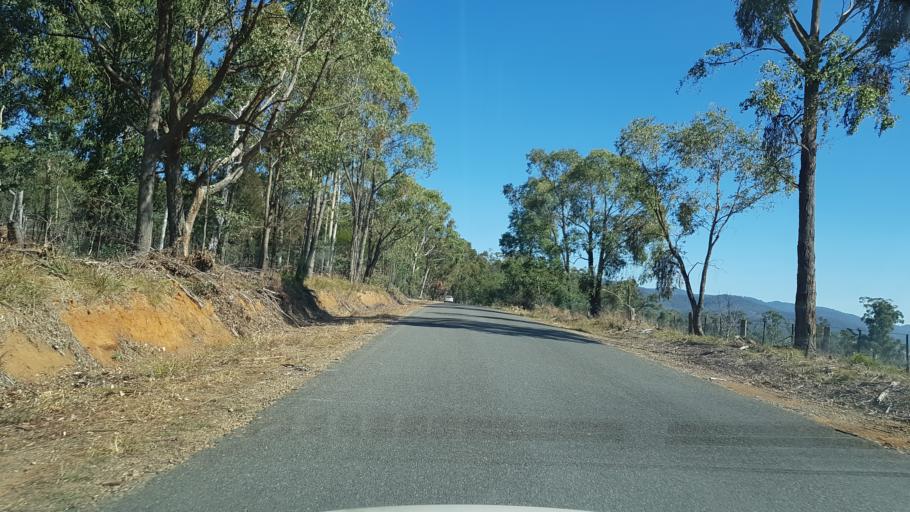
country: AU
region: Victoria
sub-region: Mansfield
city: Mansfield
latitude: -36.8149
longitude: 146.4525
